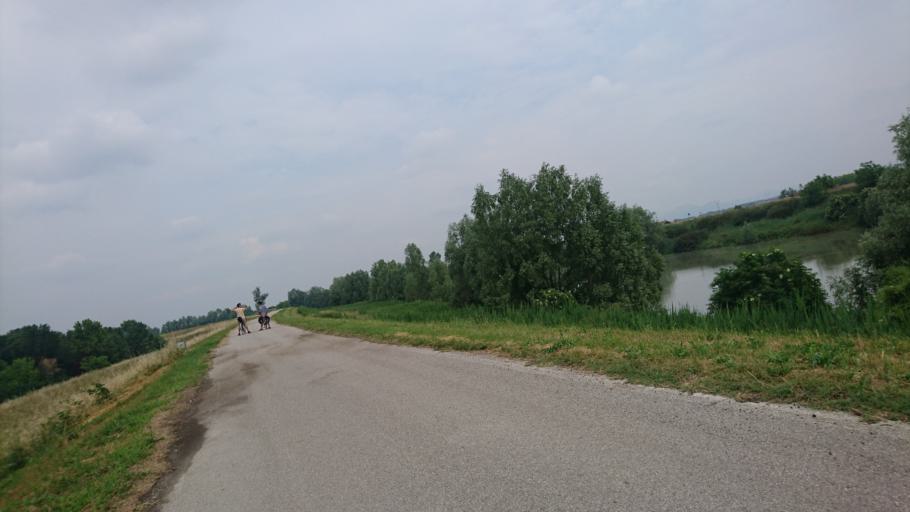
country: IT
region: Veneto
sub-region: Provincia di Padova
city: Piacenza d'Adige
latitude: 45.1197
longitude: 11.5808
